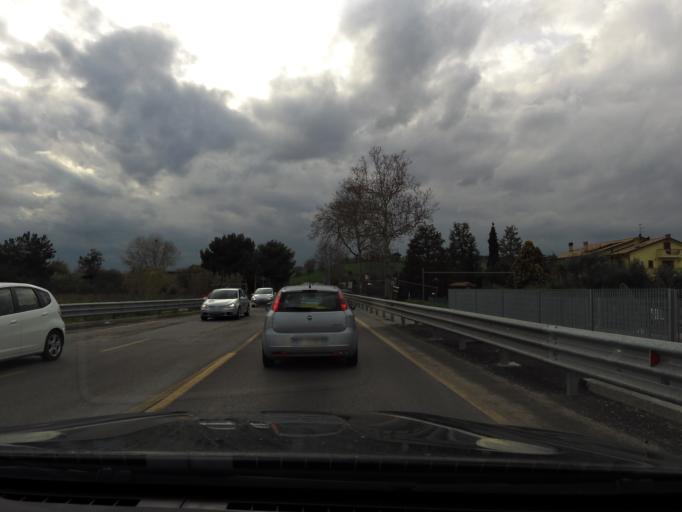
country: IT
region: The Marches
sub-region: Provincia di Macerata
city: Porto Recanati
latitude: 43.4356
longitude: 13.6568
